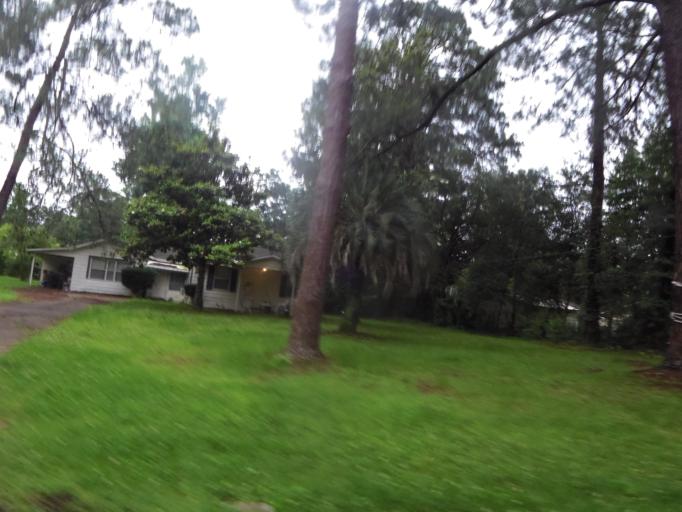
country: US
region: Florida
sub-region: Duval County
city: Jacksonville
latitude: 30.2792
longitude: -81.6249
